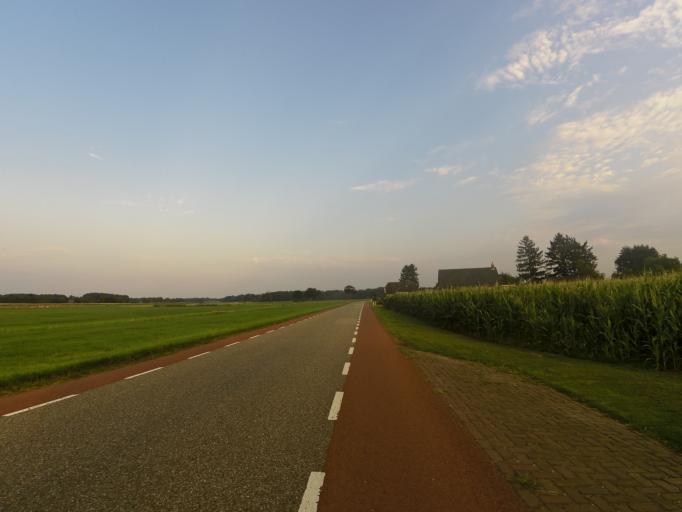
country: NL
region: Gelderland
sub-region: Oude IJsselstreek
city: Gendringen
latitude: 51.8605
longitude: 6.3881
